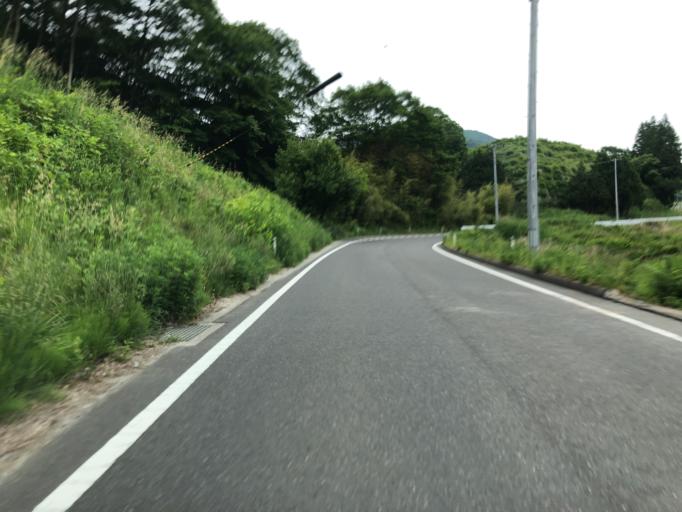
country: JP
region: Fukushima
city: Funehikimachi-funehiki
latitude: 37.3932
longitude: 140.6996
